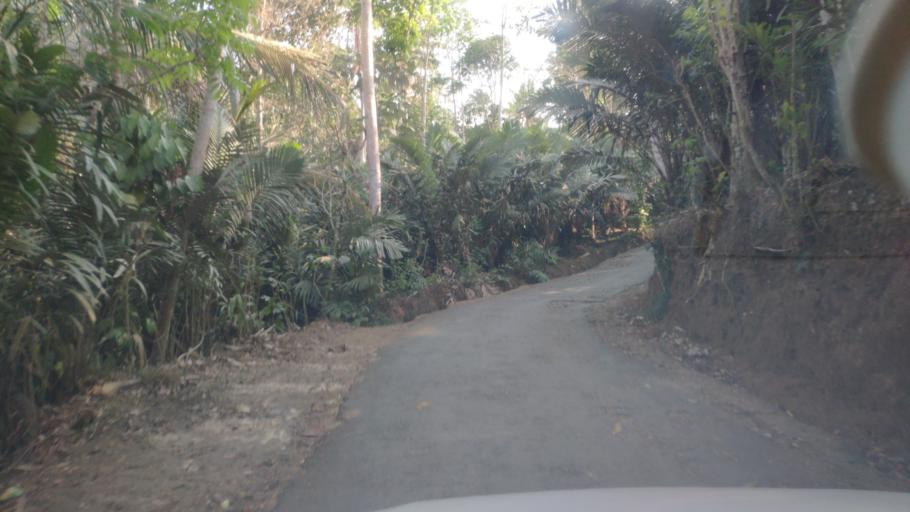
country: ID
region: Central Java
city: Wonosobo
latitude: -7.4184
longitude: 109.7387
